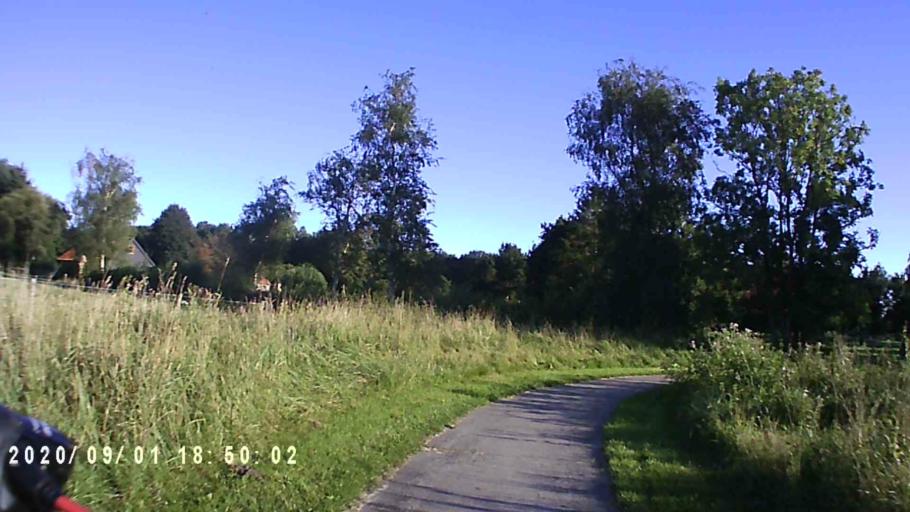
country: NL
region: Groningen
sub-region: Gemeente Veendam
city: Veendam
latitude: 53.1378
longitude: 6.8490
